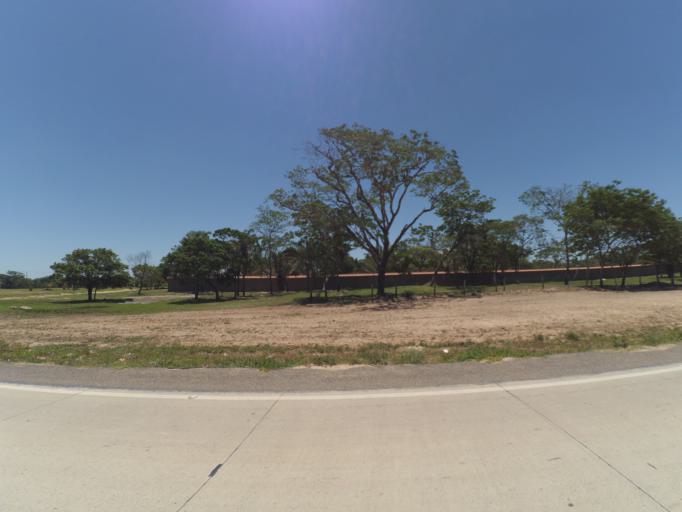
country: BO
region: Santa Cruz
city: Santa Cruz de la Sierra
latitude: -17.7775
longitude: -63.2481
